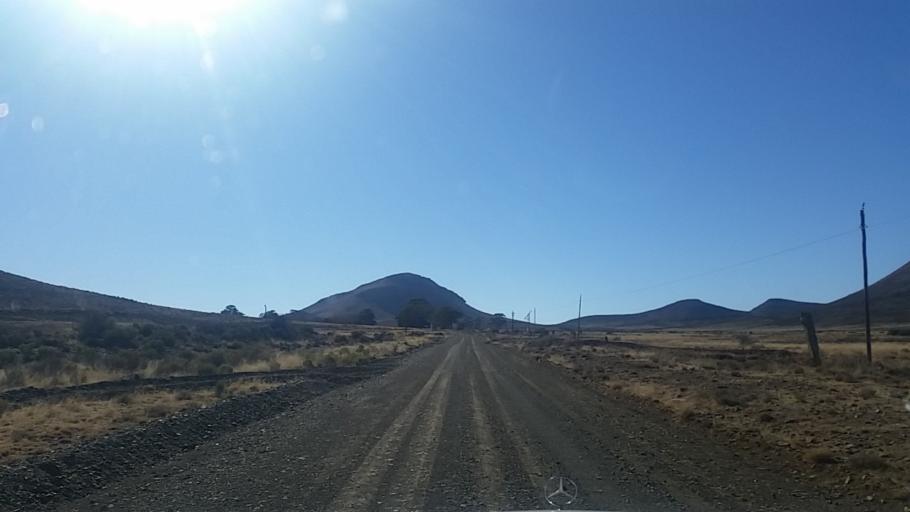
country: ZA
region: Eastern Cape
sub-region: Chris Hani District Municipality
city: Middelburg
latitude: -31.7981
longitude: 24.7233
